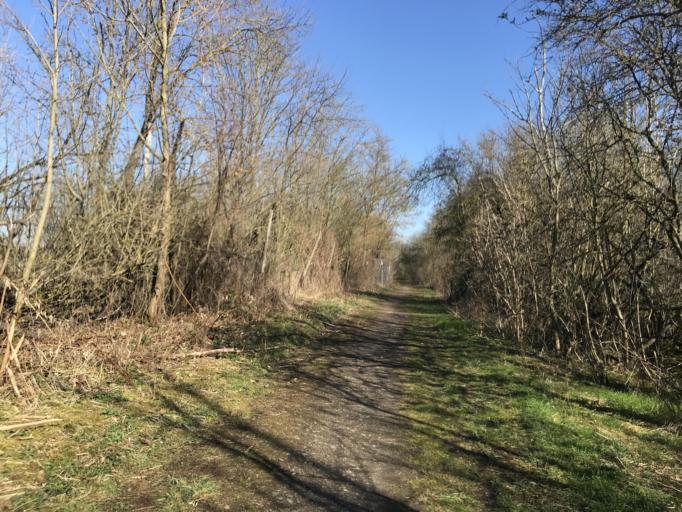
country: DE
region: Hesse
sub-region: Regierungsbezirk Darmstadt
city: Florsheim
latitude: 50.0080
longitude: 8.4050
